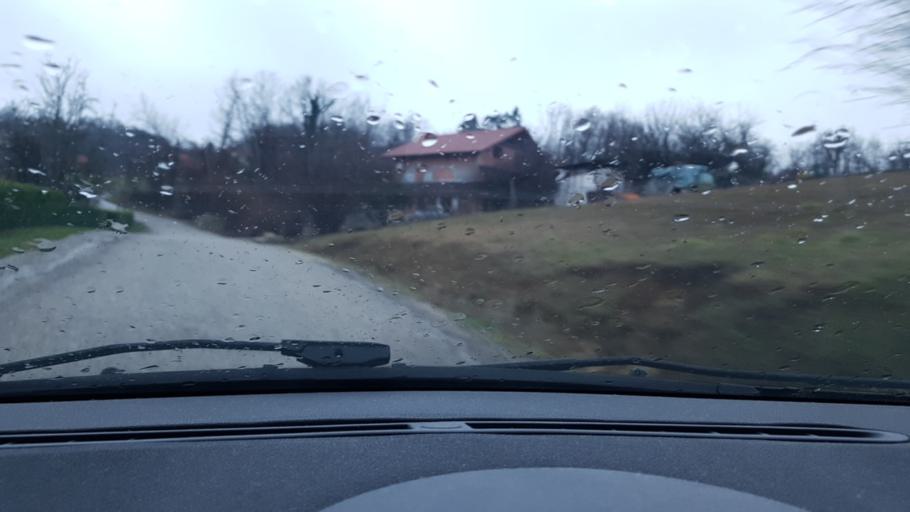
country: HR
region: Krapinsko-Zagorska
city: Bedekovcina
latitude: 45.9936
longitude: 15.9831
